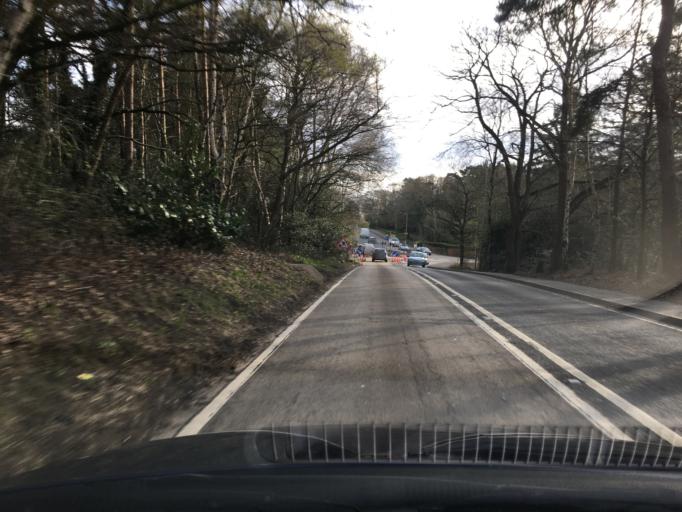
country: GB
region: England
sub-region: Bracknell Forest
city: Crowthorne
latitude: 51.3729
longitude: -0.7876
